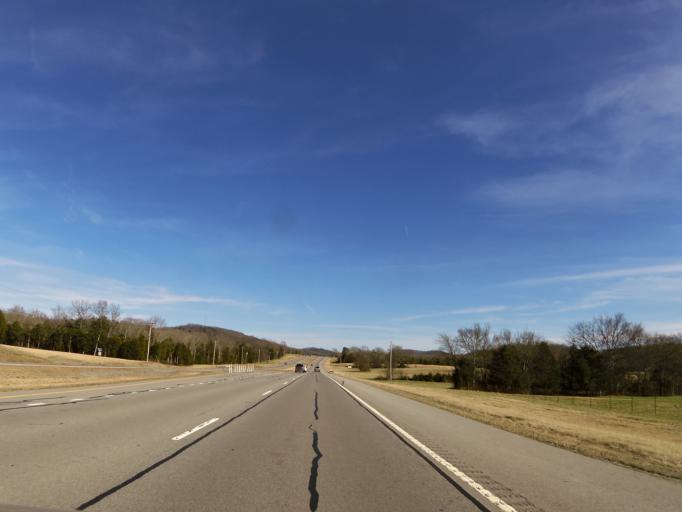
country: US
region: Tennessee
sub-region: Cannon County
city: Woodbury
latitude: 35.8172
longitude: -86.2285
